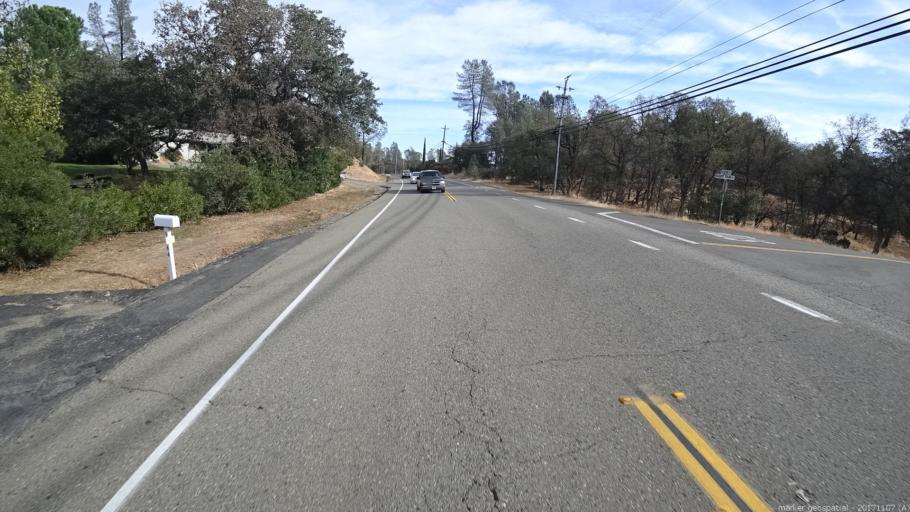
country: US
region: California
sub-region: Shasta County
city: Shasta
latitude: 40.5471
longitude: -122.4577
